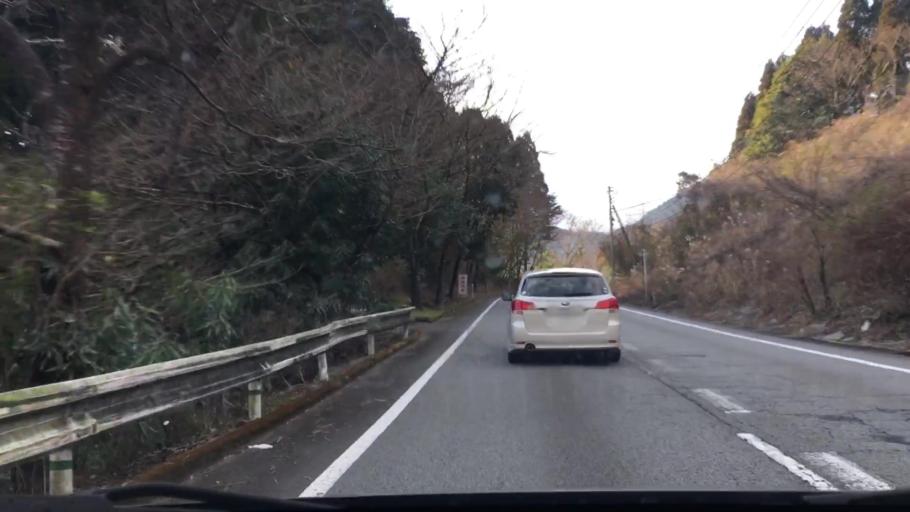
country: JP
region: Miyazaki
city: Miyazaki-shi
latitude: 31.7768
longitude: 131.3321
